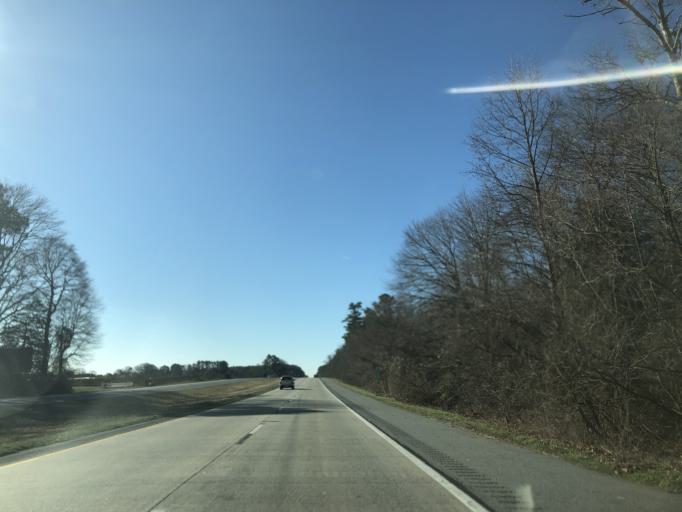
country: US
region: Delaware
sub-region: Sussex County
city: Milford
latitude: 38.8780
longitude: -75.4396
